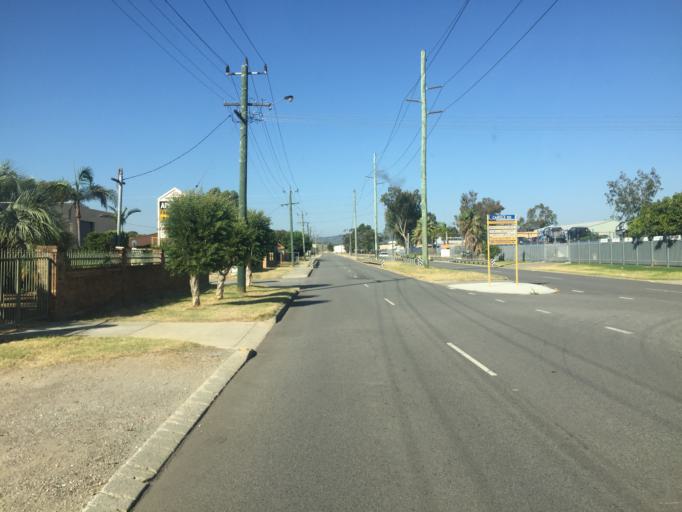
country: AU
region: Western Australia
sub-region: Gosnells
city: Maddington
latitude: -32.0440
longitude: 115.9786
